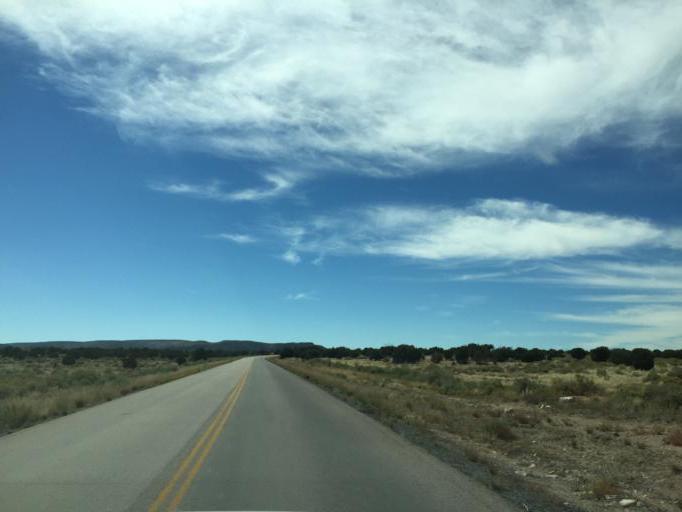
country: US
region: Arizona
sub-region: Mohave County
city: Meadview
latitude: 35.9588
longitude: -113.8385
